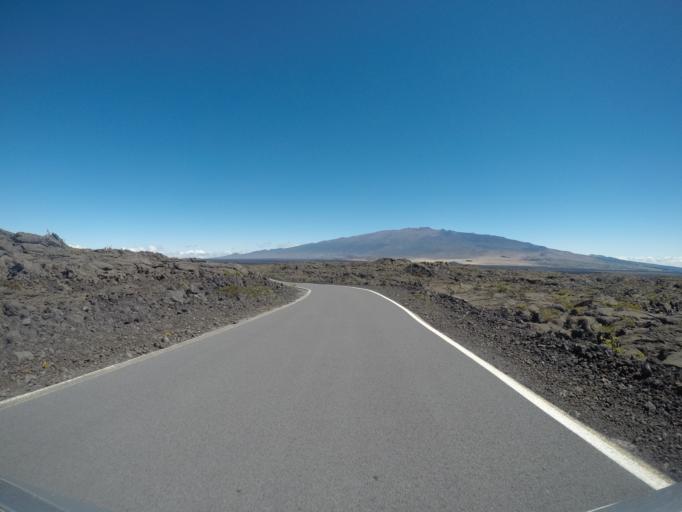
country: US
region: Hawaii
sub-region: Hawaii County
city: Volcano
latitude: 19.6223
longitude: -155.4743
